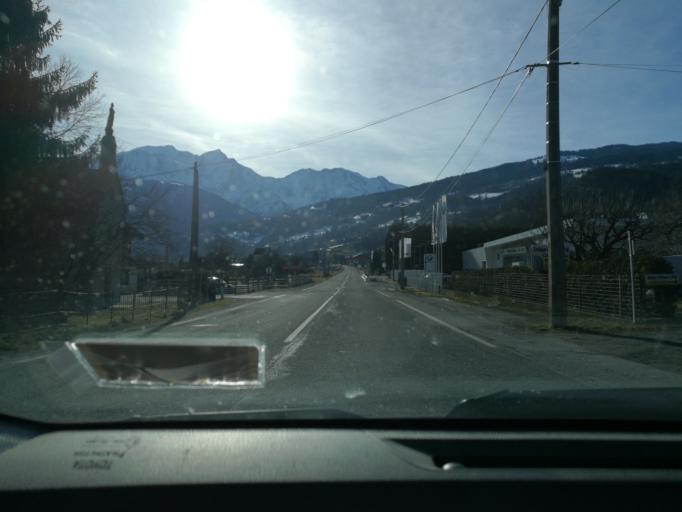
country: FR
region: Rhone-Alpes
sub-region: Departement de la Haute-Savoie
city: Domancy
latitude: 45.9154
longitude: 6.6498
